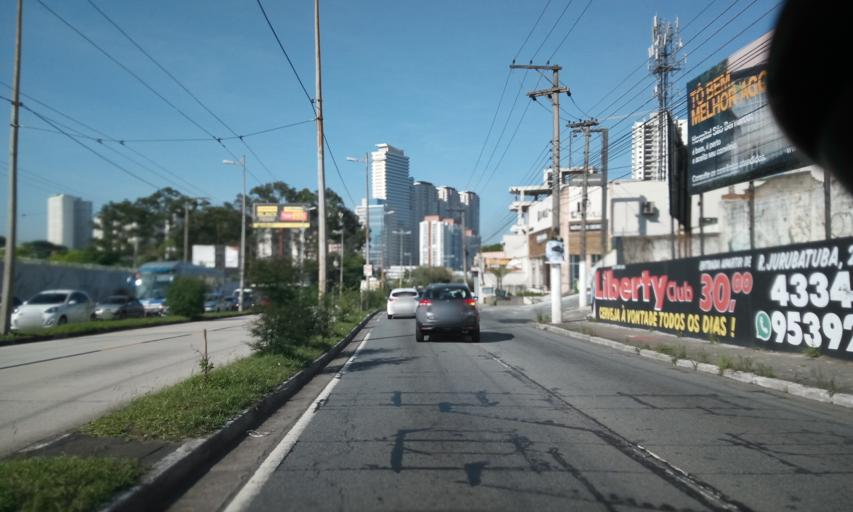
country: BR
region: Sao Paulo
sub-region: Santo Andre
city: Santo Andre
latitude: -23.6820
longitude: -46.5429
